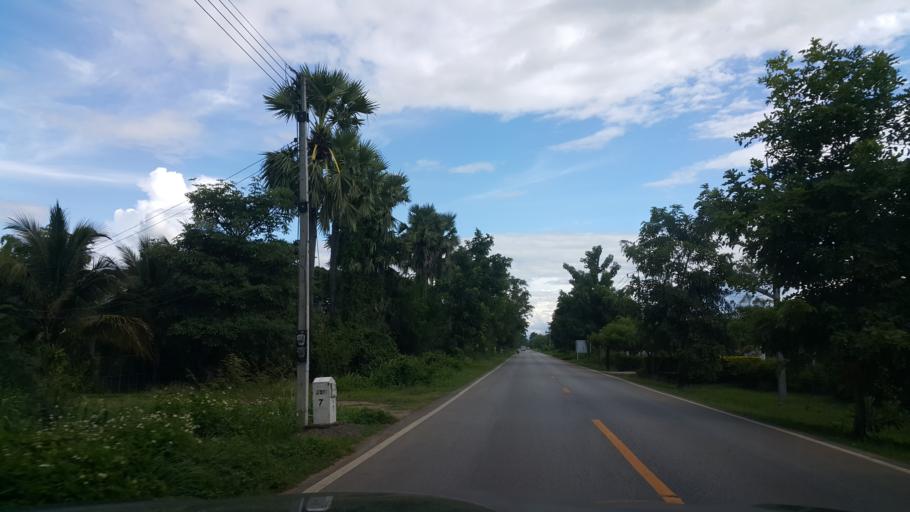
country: TH
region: Lampang
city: Ko Kha
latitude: 18.2430
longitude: 99.3893
